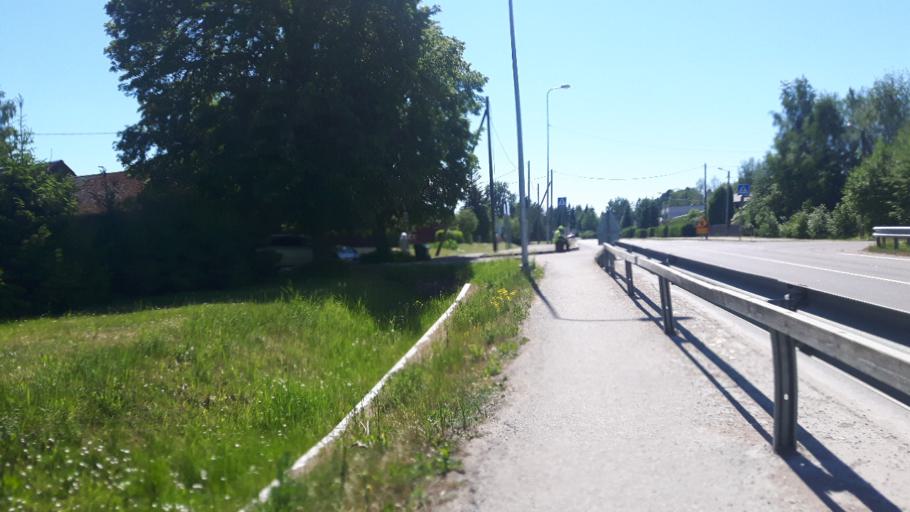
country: EE
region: Harju
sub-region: Saku vald
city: Saku
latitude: 59.2325
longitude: 24.6811
